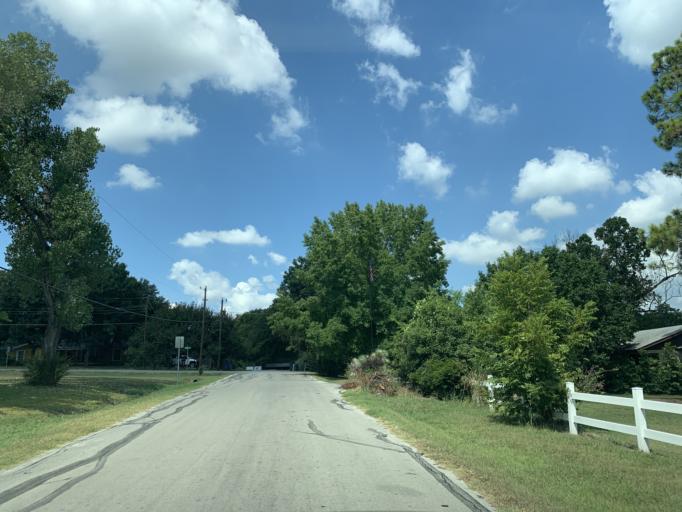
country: US
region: Texas
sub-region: Tarrant County
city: Azle
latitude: 32.8859
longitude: -97.5412
